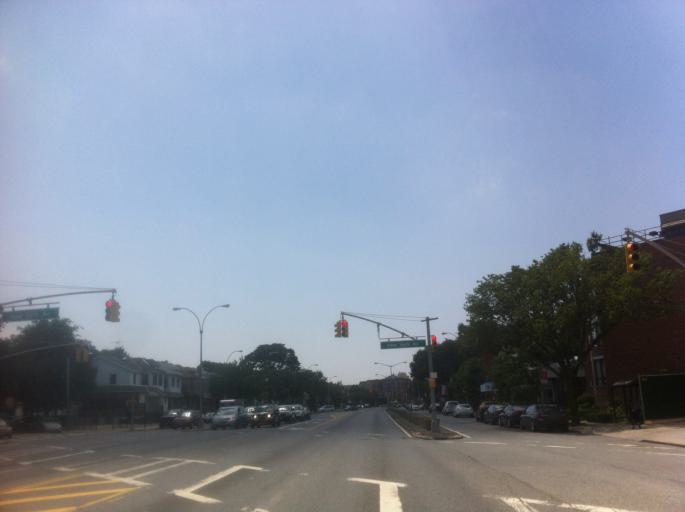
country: US
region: New York
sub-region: Kings County
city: Brooklyn
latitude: 40.6197
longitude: -73.9417
